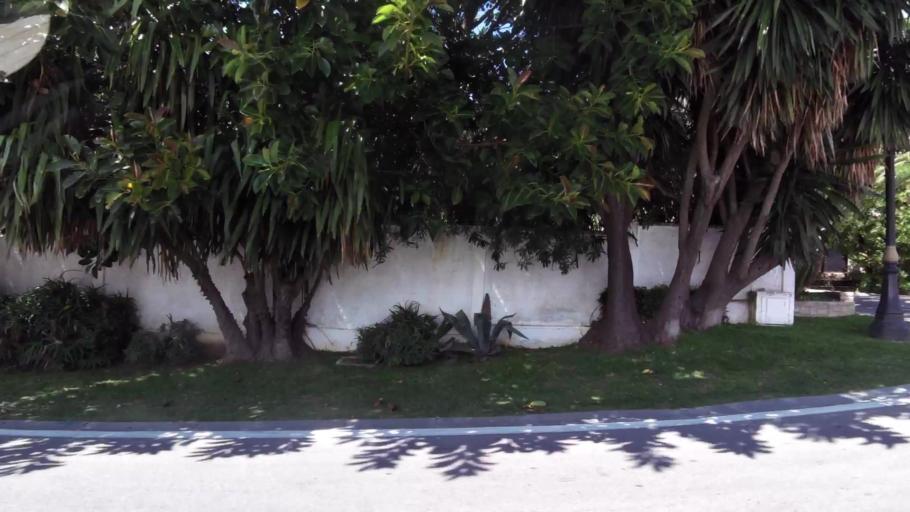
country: MA
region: Tanger-Tetouan
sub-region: Tanger-Assilah
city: Tangier
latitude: 35.7897
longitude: -5.8413
